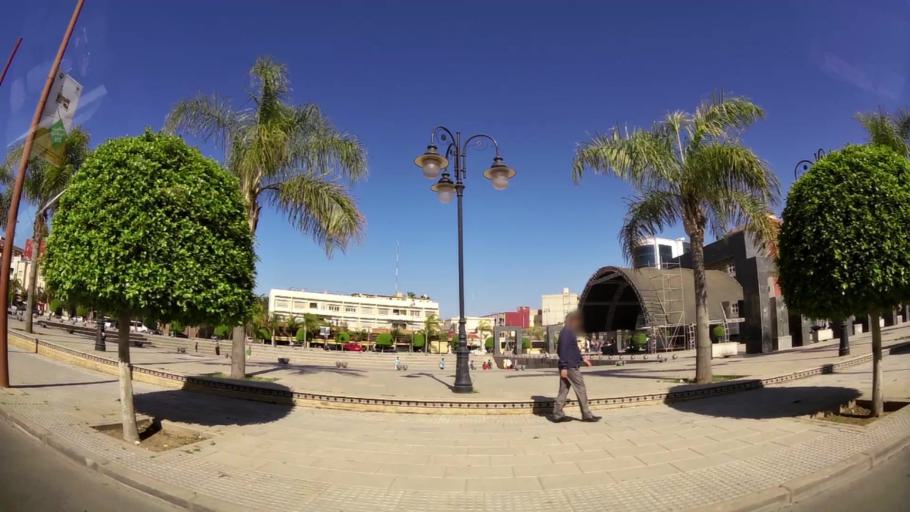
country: MA
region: Oriental
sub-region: Oujda-Angad
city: Oujda
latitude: 34.6907
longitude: -1.9187
